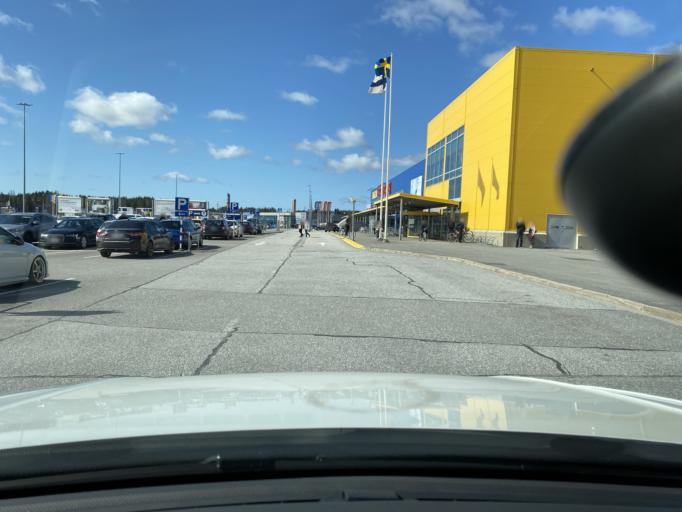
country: FI
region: Varsinais-Suomi
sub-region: Turku
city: Rusko
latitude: 60.4942
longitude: 22.2300
